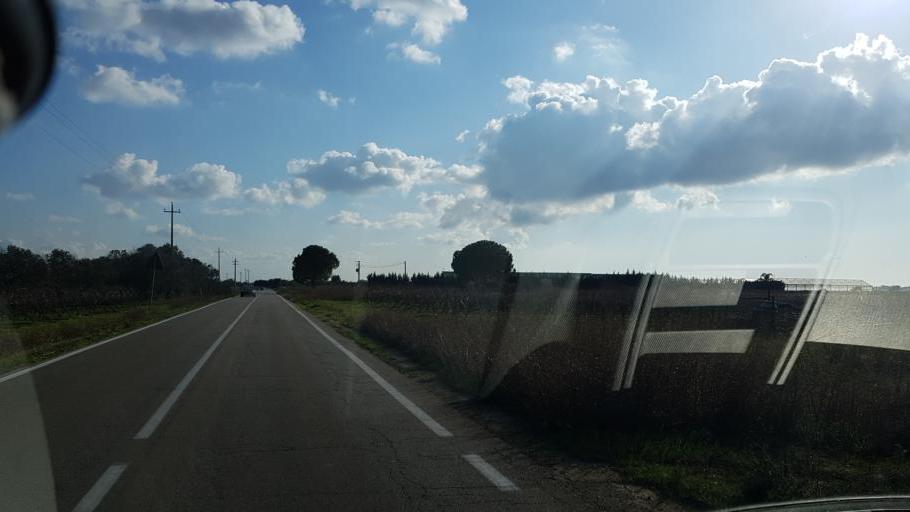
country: IT
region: Apulia
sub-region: Provincia di Lecce
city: Veglie
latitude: 40.3153
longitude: 17.9821
